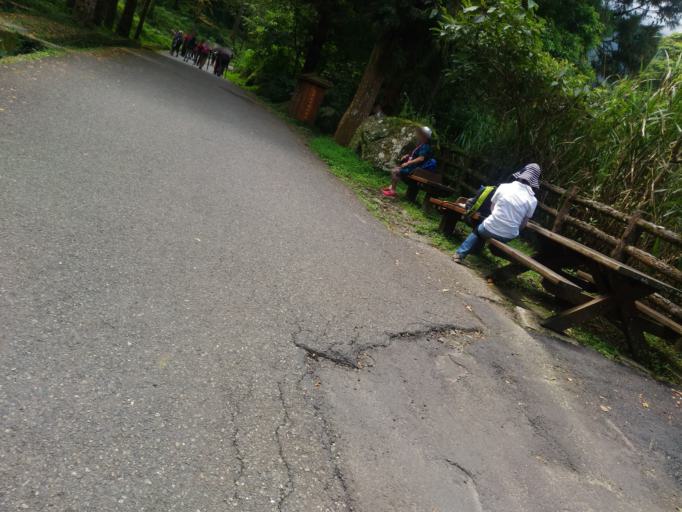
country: TW
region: Taiwan
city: Lugu
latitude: 23.6672
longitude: 120.7982
